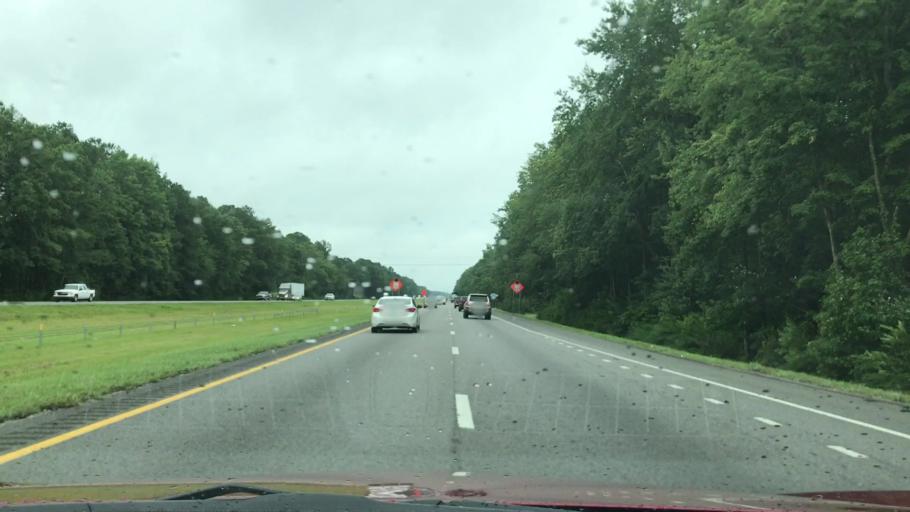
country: US
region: South Carolina
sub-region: Dorchester County
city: Ridgeville
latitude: 33.1343
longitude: -80.3051
